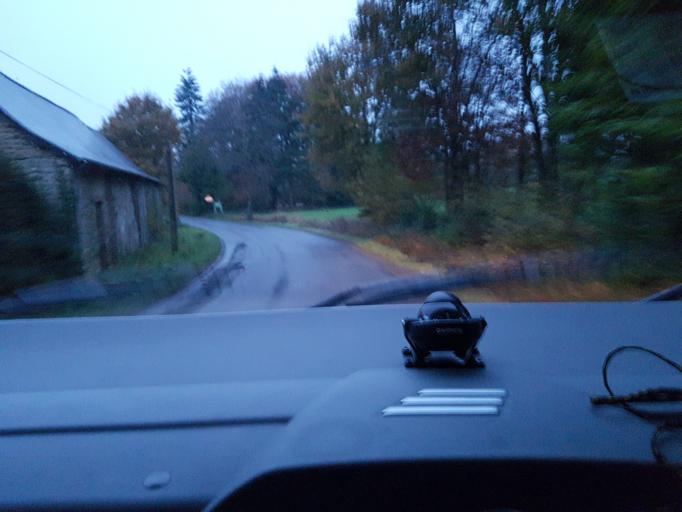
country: FR
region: Brittany
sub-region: Departement d'Ille-et-Vilaine
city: Livre-sur-Changeon
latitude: 48.1819
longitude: -1.2976
